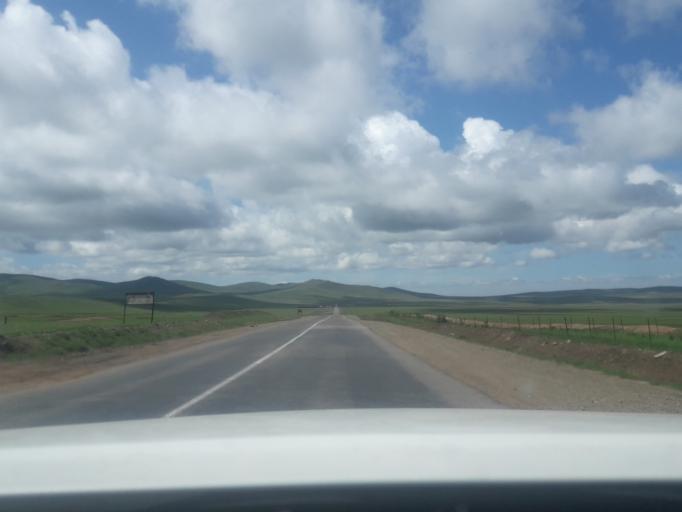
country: MN
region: Central Aimak
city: Altanbulag
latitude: 47.9008
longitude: 106.4740
